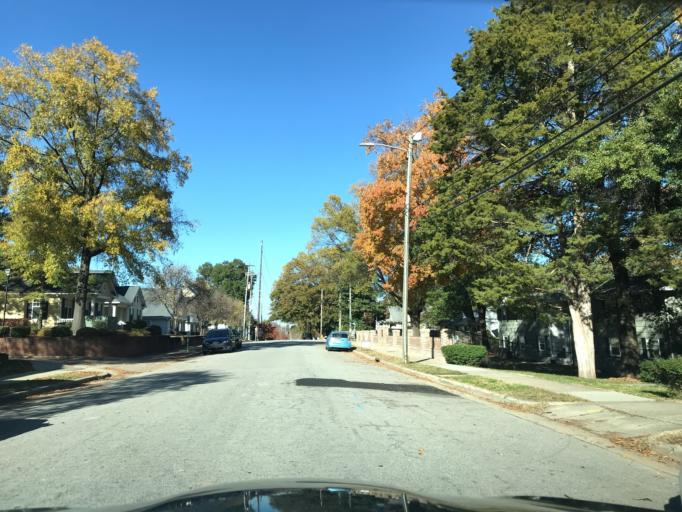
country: US
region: North Carolina
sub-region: Wake County
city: Raleigh
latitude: 35.7926
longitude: -78.6357
